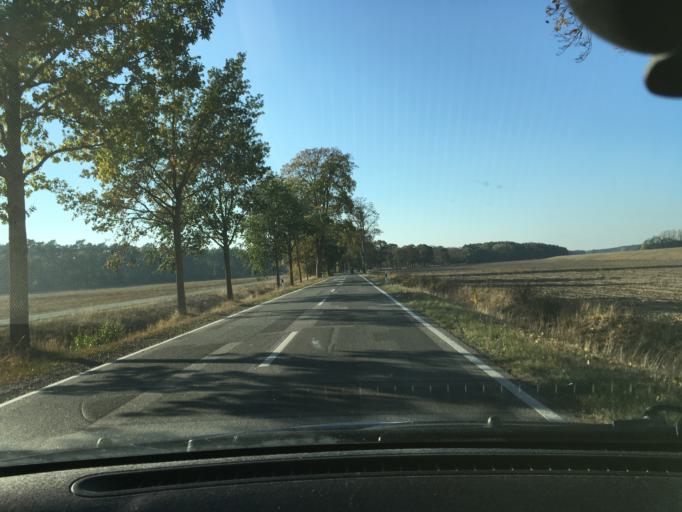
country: DE
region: Mecklenburg-Vorpommern
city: Domitz
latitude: 53.1537
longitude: 11.2212
